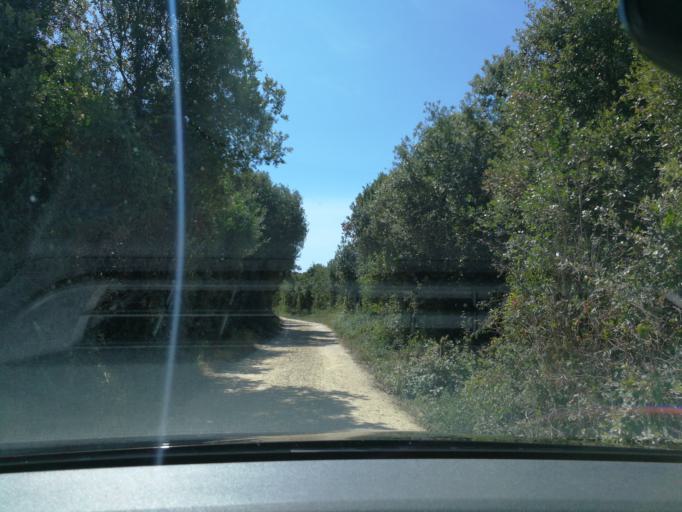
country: HR
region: Istarska
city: Medulin
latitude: 44.8102
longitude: 13.8788
